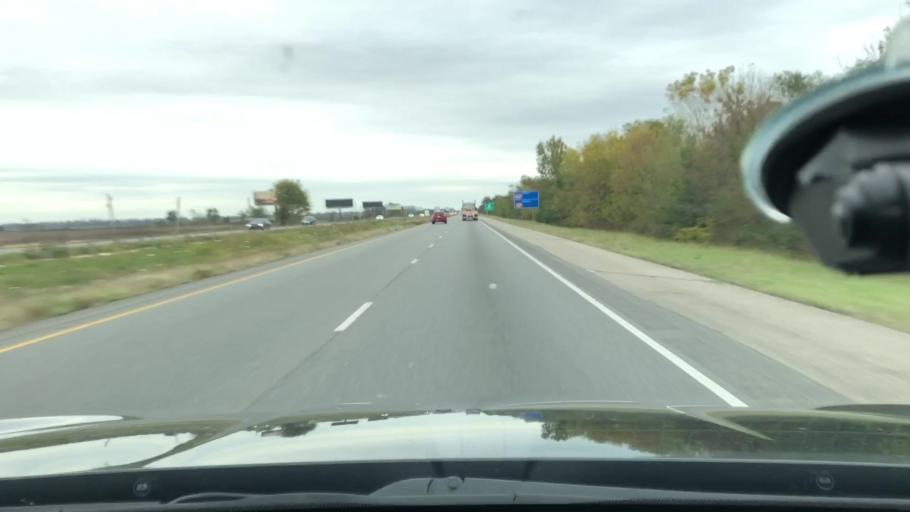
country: US
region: Arkansas
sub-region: Miller County
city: Texarkana
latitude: 33.4955
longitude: -93.9639
